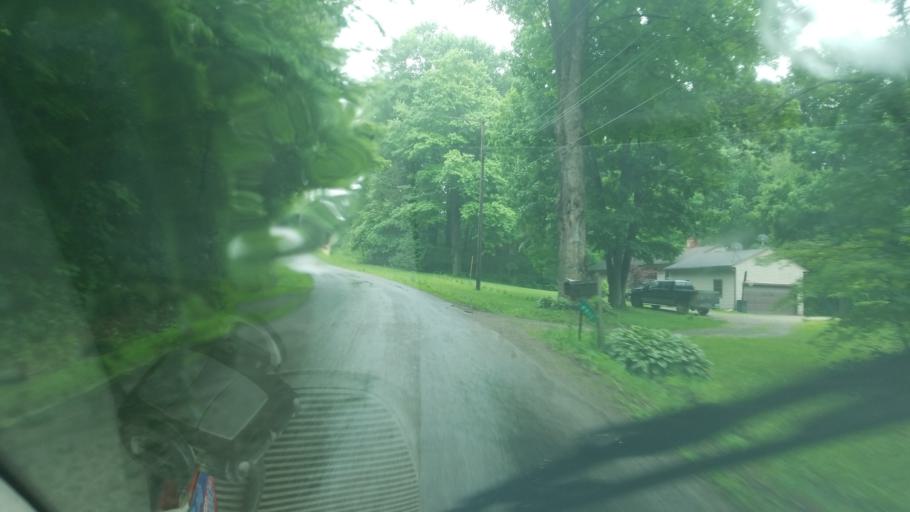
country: US
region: Ohio
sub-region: Sandusky County
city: Bellville
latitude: 40.6248
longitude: -82.4301
